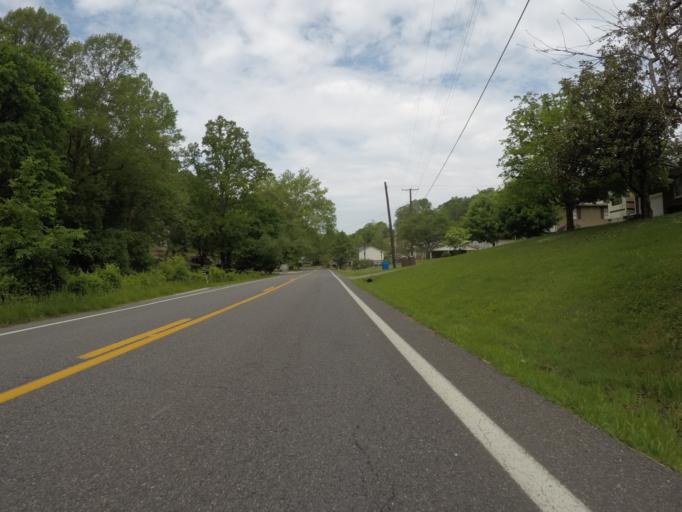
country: US
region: West Virginia
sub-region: Wayne County
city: Ceredo
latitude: 38.3553
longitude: -82.5555
